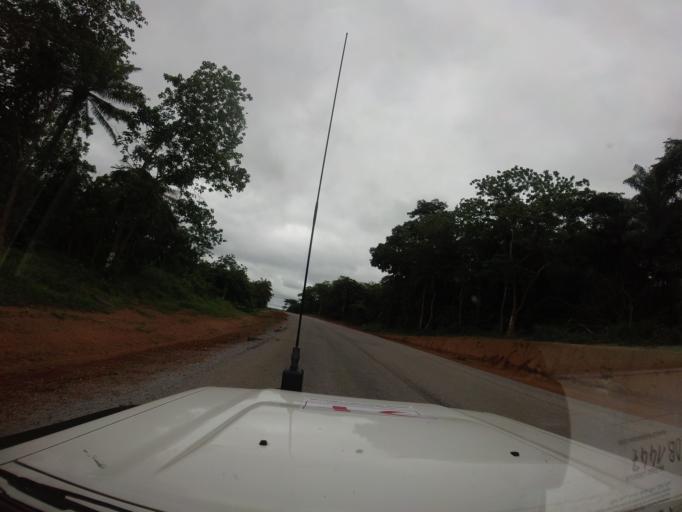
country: GN
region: Faranah
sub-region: Kissidougou
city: Kissidougou
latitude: 9.0594
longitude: -10.0902
